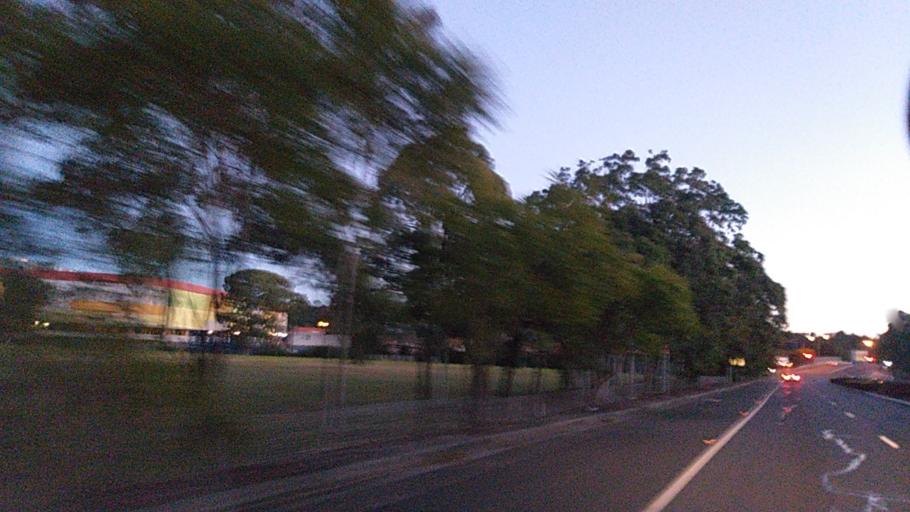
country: AU
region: New South Wales
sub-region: Campbelltown Municipality
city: Campbelltown
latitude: -34.0597
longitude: 150.8246
